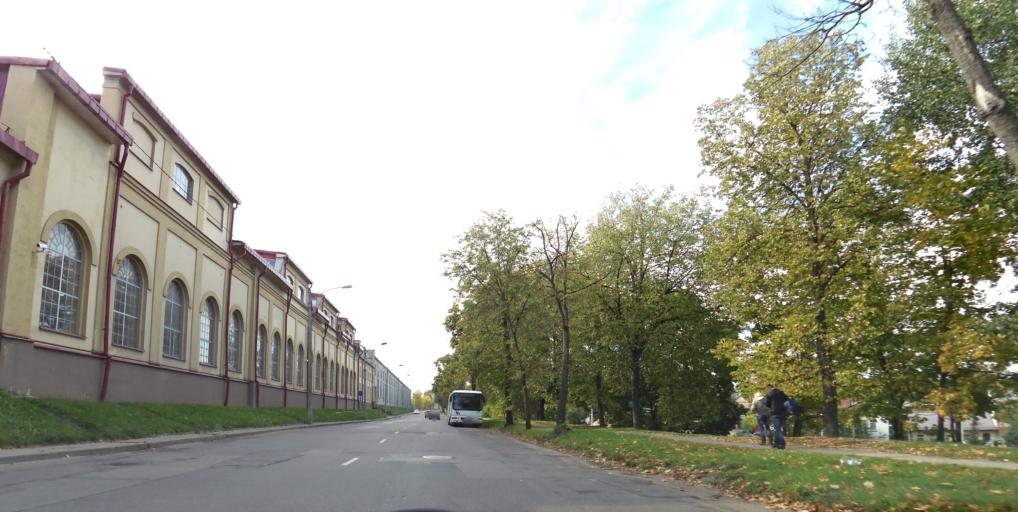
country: LT
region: Vilnius County
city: Naujamiestis
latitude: 54.6692
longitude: 25.2797
